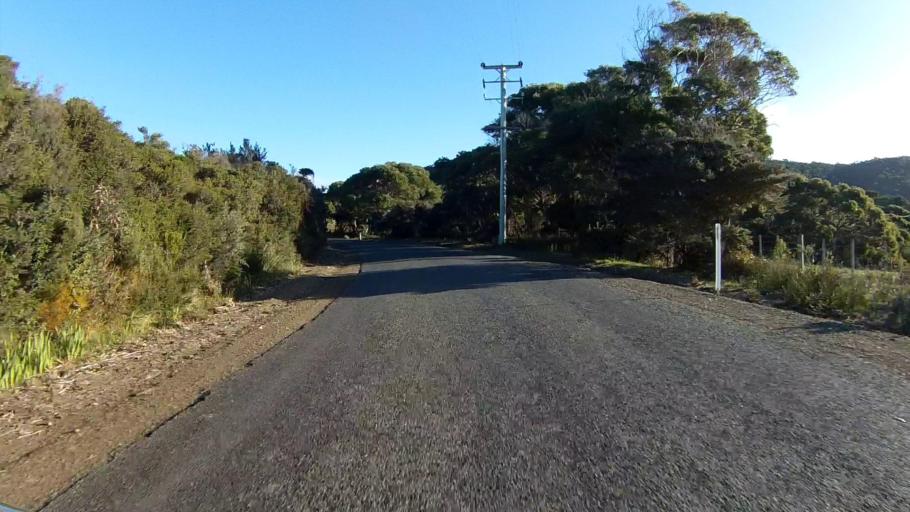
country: AU
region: Tasmania
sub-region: Clarence
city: Sandford
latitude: -43.1843
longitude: 147.8500
